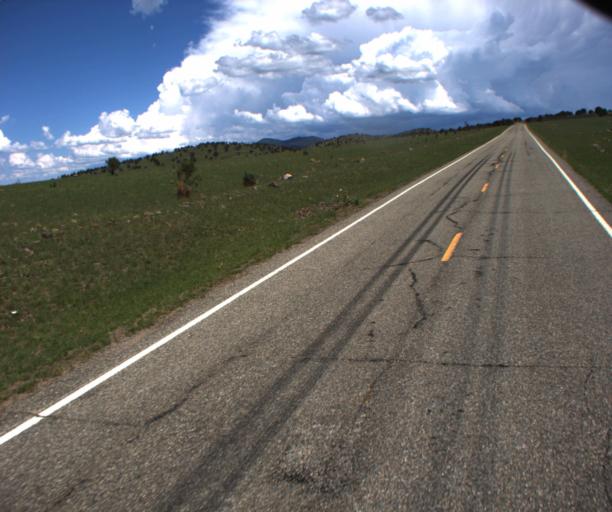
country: US
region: Arizona
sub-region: Greenlee County
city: Morenci
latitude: 33.3332
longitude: -109.3489
